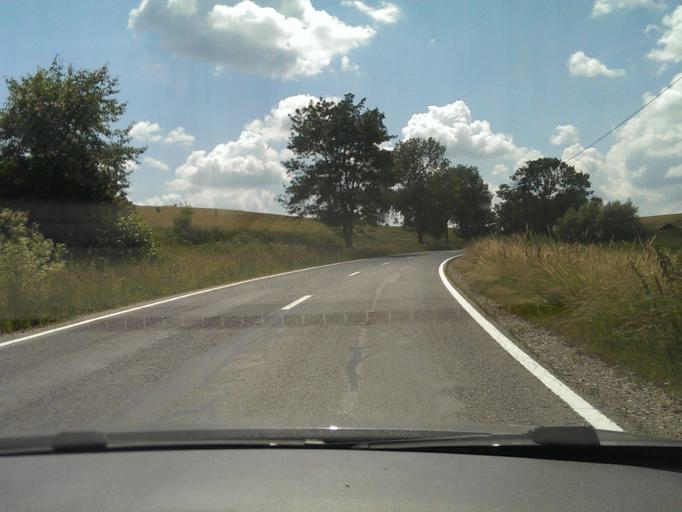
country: RO
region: Cluj
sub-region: Comuna Apahida
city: Apahida
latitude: 46.8082
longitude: 23.7803
